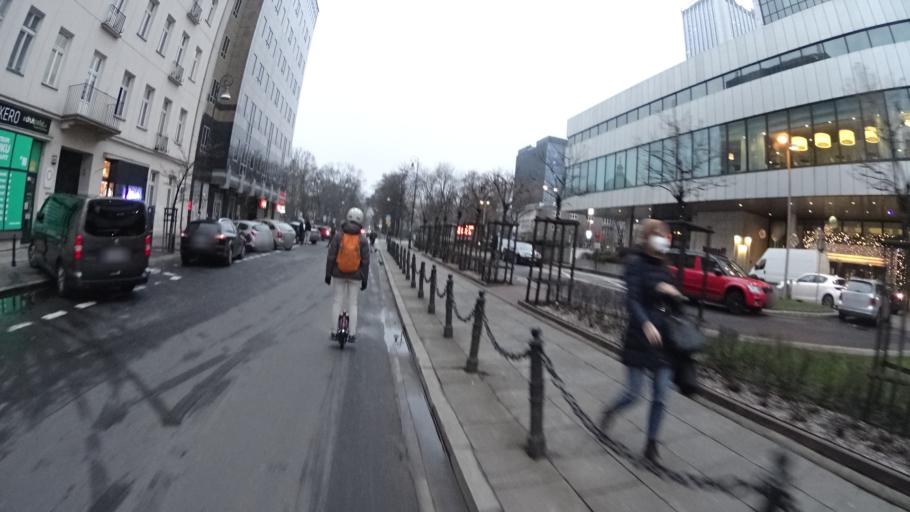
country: PL
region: Masovian Voivodeship
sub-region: Warszawa
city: Warsaw
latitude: 52.2281
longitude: 21.0057
